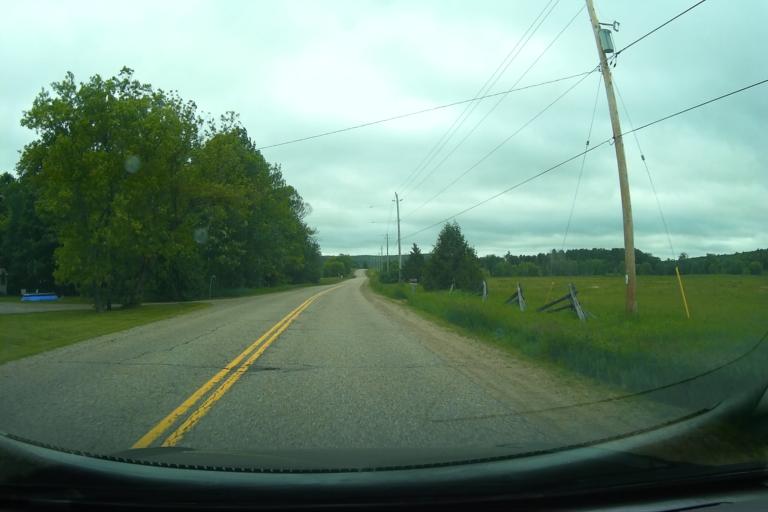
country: CA
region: Ontario
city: Pembroke
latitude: 45.4616
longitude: -77.2635
